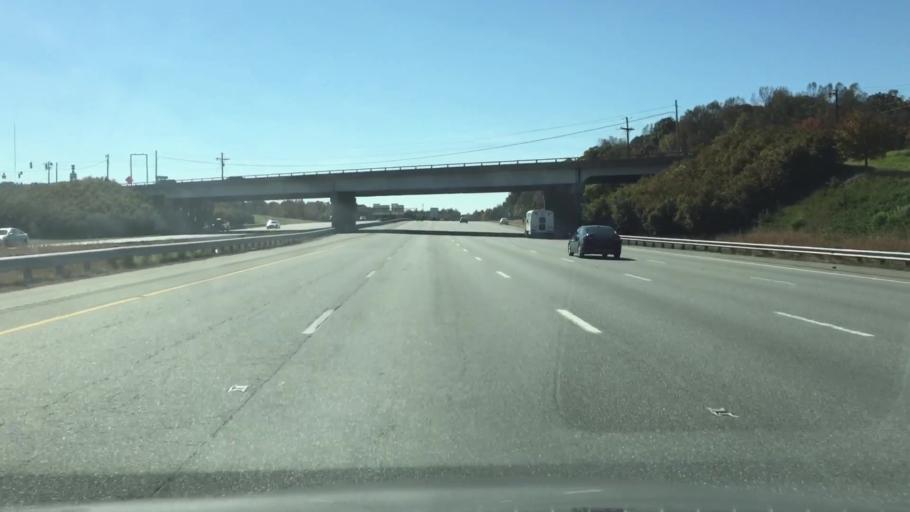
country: US
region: North Carolina
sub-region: Guilford County
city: Jamestown
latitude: 35.9984
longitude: -79.8638
